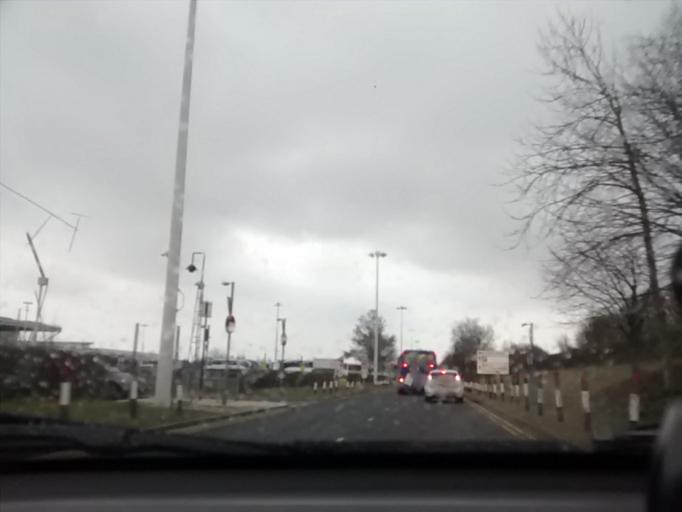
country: GB
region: England
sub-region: Essex
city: Takeley
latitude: 51.8879
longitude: 0.2632
